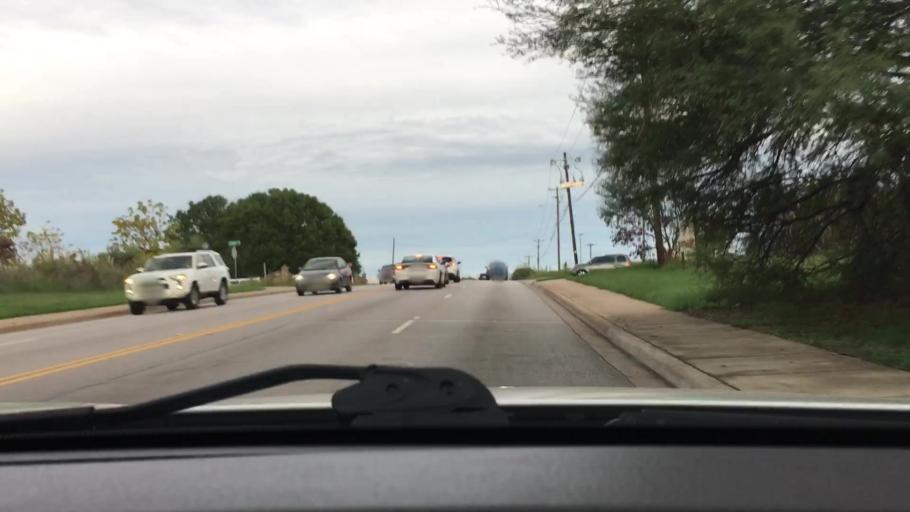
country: US
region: Texas
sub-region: Williamson County
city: Round Rock
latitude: 30.4963
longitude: -97.6504
